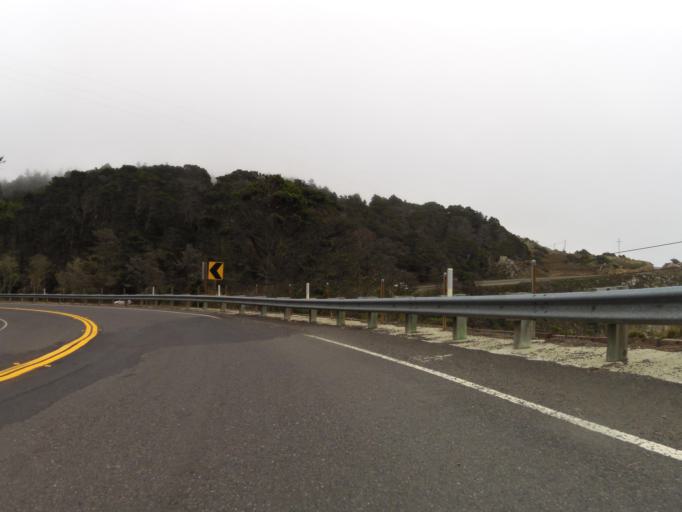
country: US
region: California
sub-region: Sonoma County
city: Monte Rio
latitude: 38.5251
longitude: -123.2659
